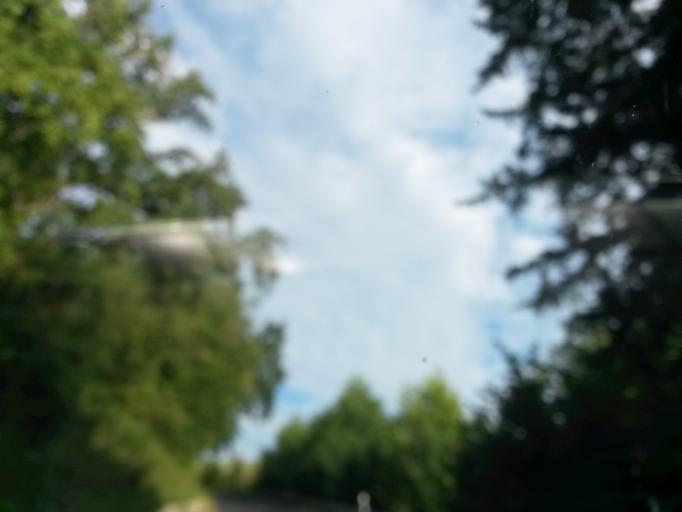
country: DE
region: North Rhine-Westphalia
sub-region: Regierungsbezirk Koln
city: Rosrath
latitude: 50.8895
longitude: 7.2145
